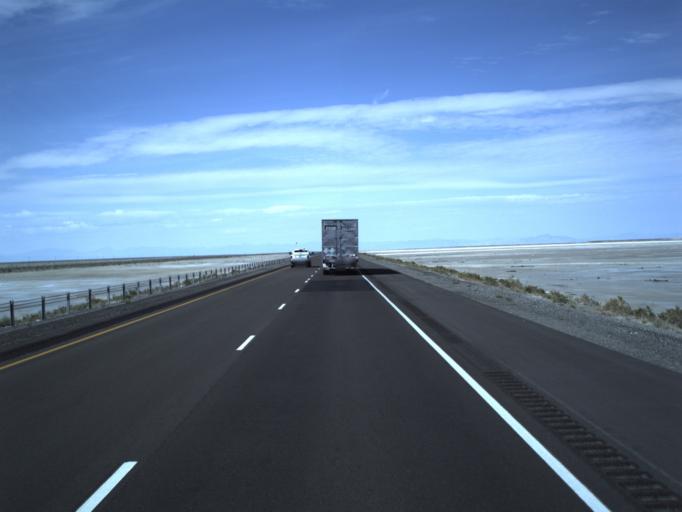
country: US
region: Utah
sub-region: Tooele County
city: Wendover
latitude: 40.7285
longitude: -113.3320
